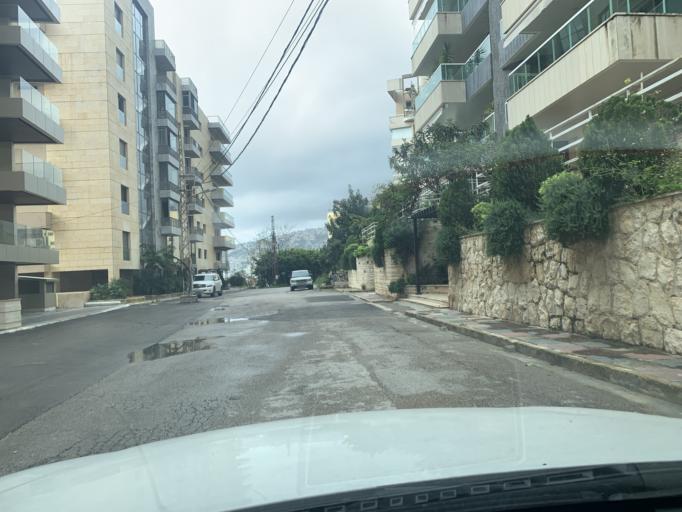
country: LB
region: Mont-Liban
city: Djounie
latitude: 34.0005
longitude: 35.6520
